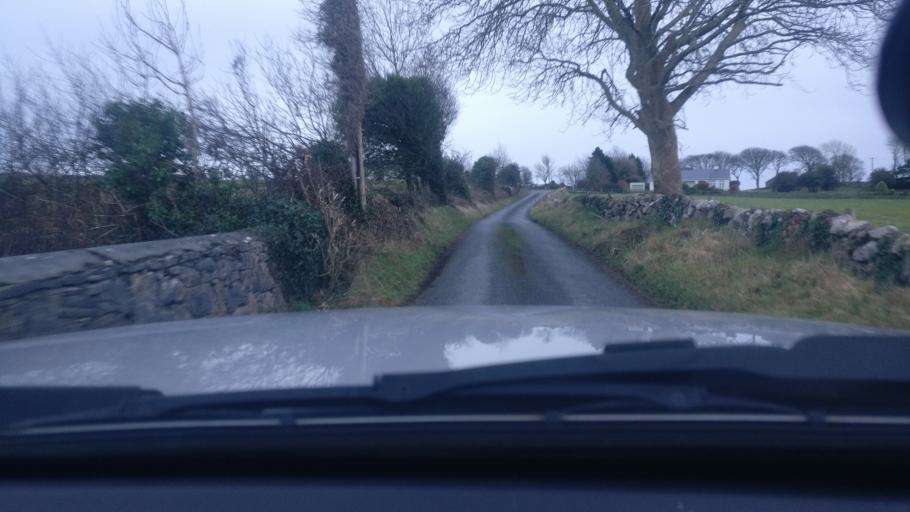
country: IE
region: Connaught
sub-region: County Galway
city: Loughrea
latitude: 53.1858
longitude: -8.6098
